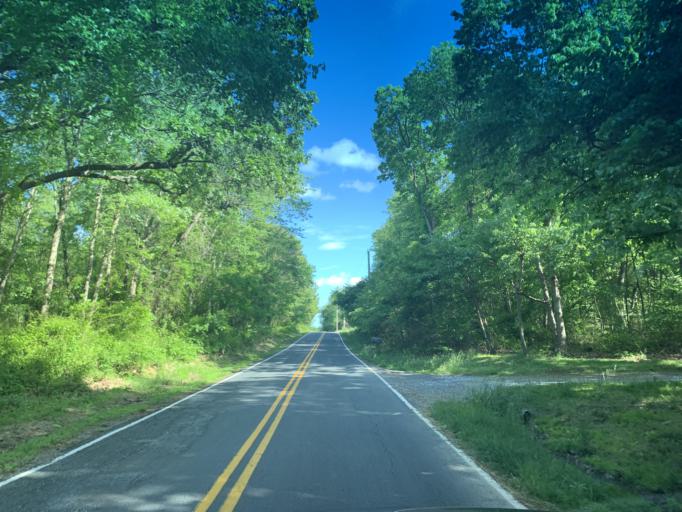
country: US
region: Maryland
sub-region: Cecil County
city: Rising Sun
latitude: 39.7128
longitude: -76.1858
